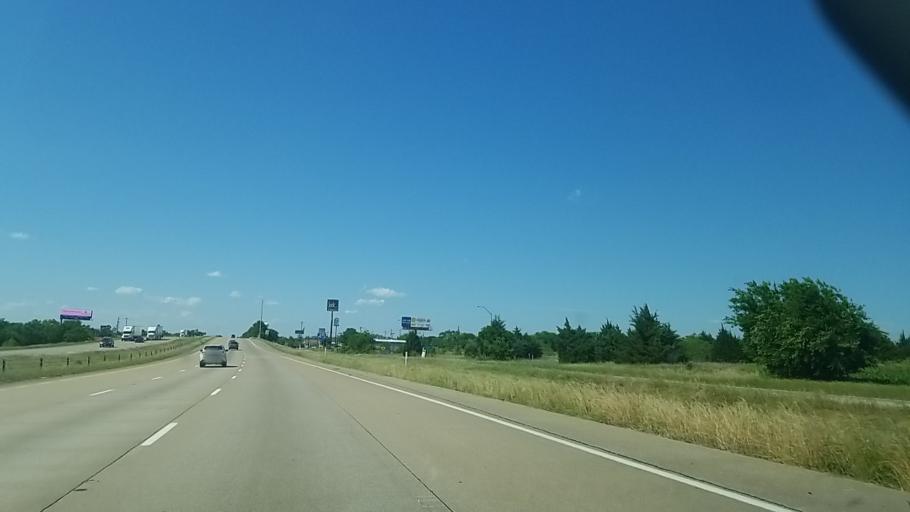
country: US
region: Texas
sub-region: Ellis County
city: Ferris
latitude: 32.5281
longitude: -96.6591
